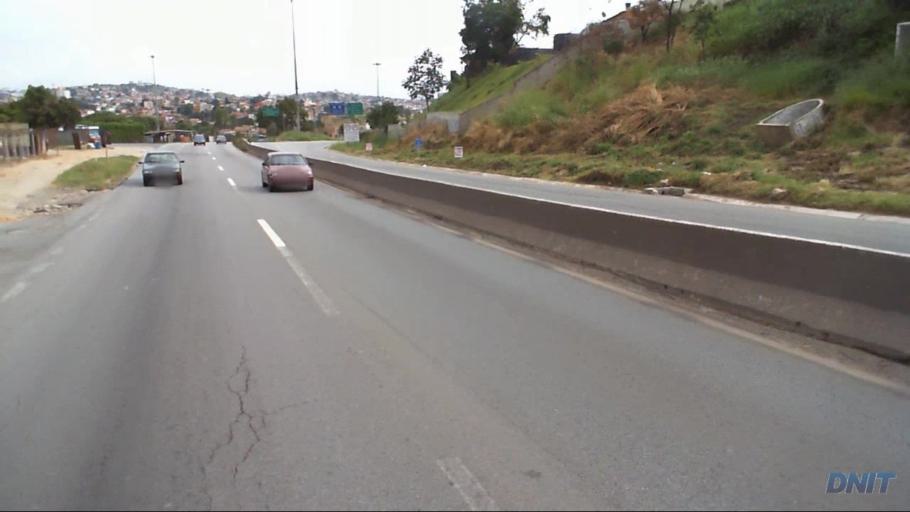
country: BR
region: Minas Gerais
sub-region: Belo Horizonte
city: Belo Horizonte
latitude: -19.8539
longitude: -43.8904
